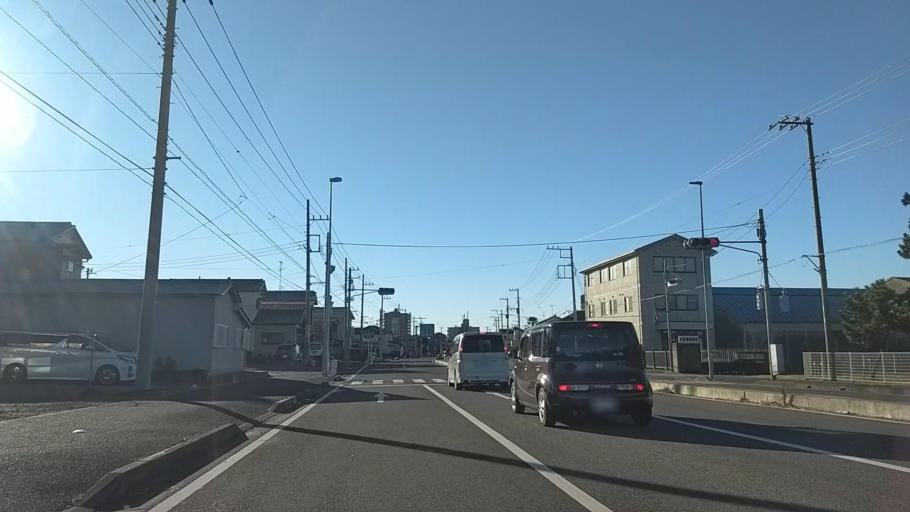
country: JP
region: Chiba
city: Kisarazu
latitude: 35.3884
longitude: 139.9201
